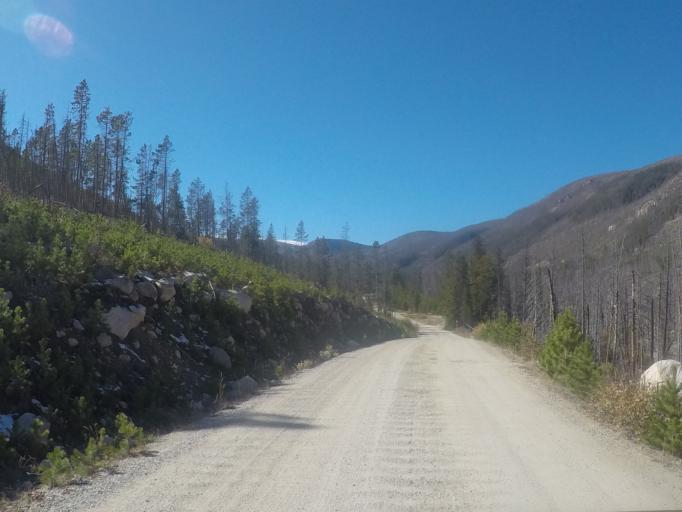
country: US
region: Montana
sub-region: Carbon County
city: Red Lodge
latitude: 45.1705
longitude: -109.4226
